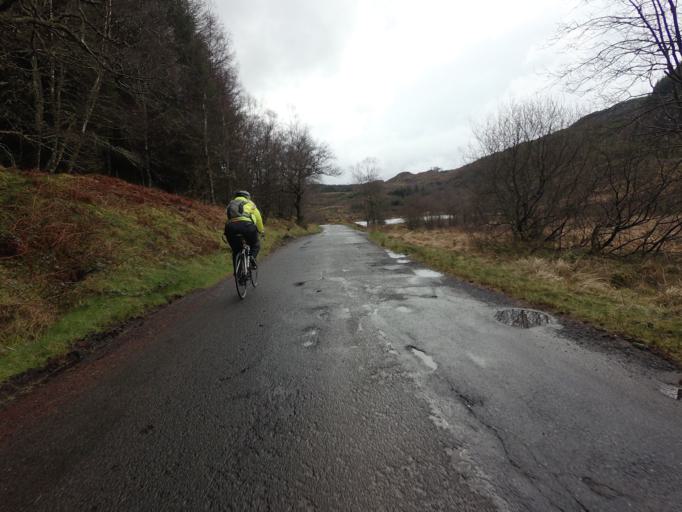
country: GB
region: Scotland
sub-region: West Dunbartonshire
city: Balloch
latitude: 56.2034
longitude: -4.5292
